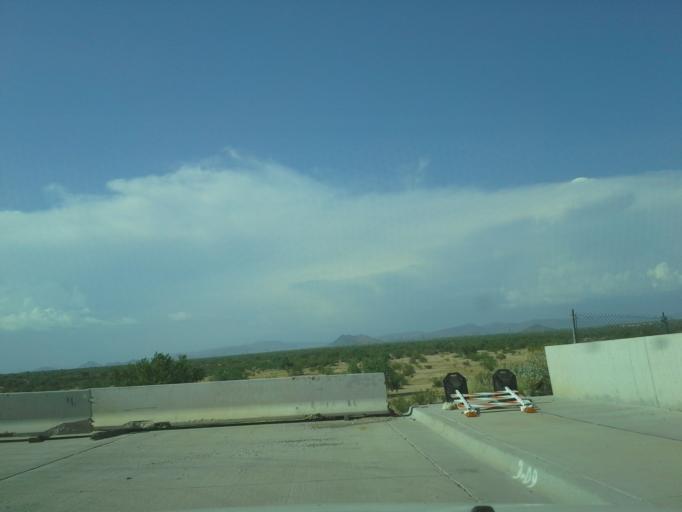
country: US
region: Arizona
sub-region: Maricopa County
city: Paradise Valley
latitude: 33.6629
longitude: -111.9425
